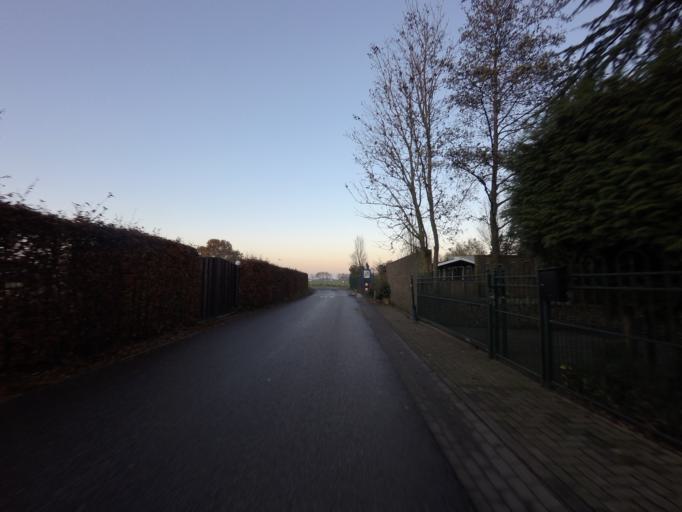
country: NL
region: Gelderland
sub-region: Gemeente Maasdriel
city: Hedel
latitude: 51.7593
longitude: 5.2272
